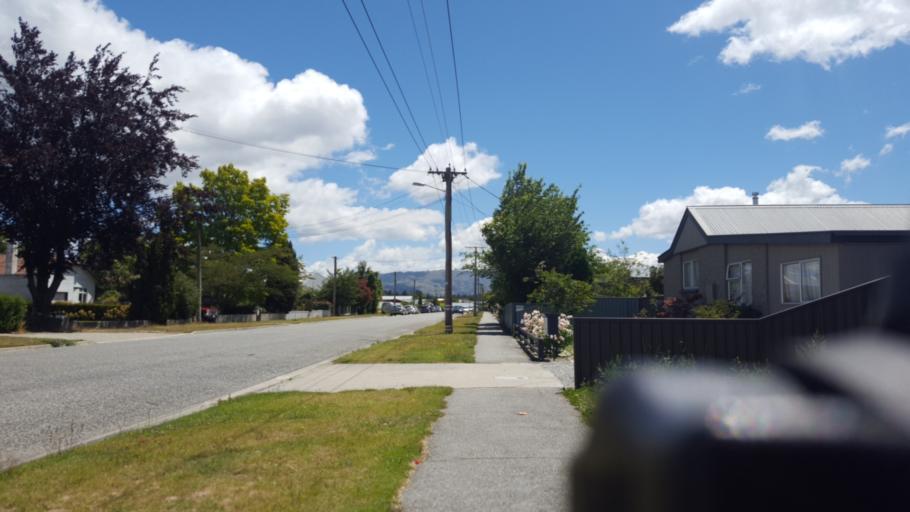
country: NZ
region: Otago
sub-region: Queenstown-Lakes District
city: Wanaka
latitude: -45.2504
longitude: 169.3893
